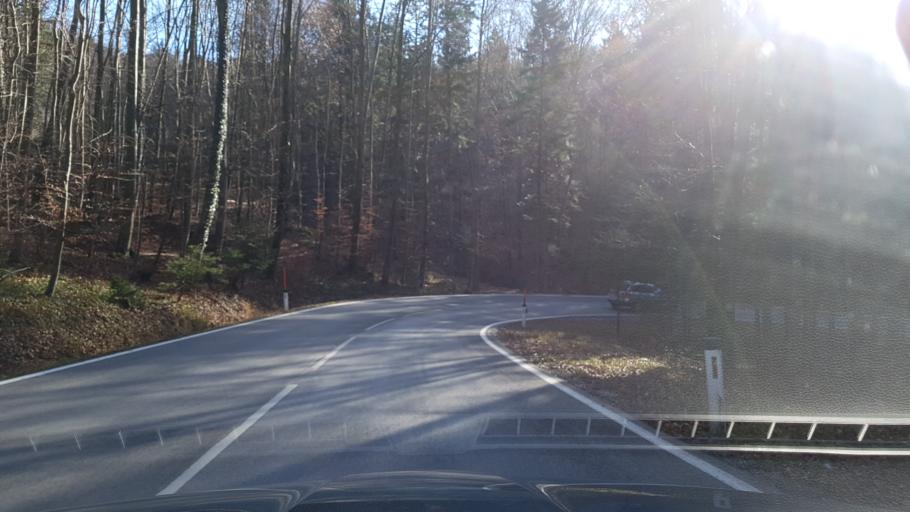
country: AT
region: Salzburg
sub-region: Politischer Bezirk Salzburg-Umgebung
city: Elsbethen
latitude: 47.7728
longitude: 13.0932
